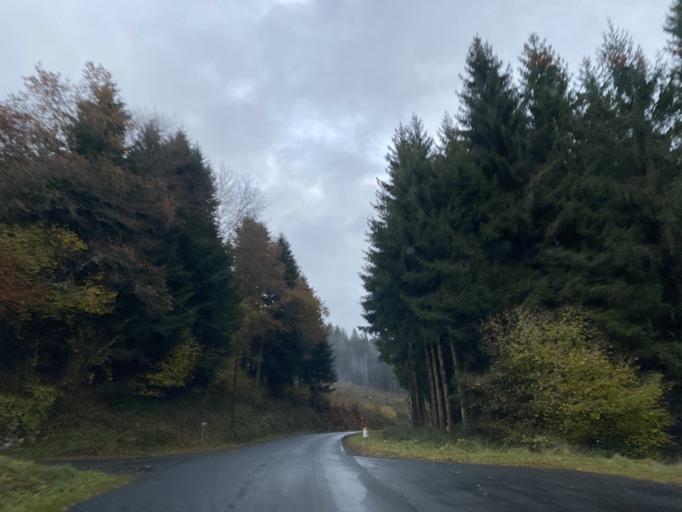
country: FR
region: Auvergne
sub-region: Departement du Puy-de-Dome
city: Cunlhat
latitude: 45.5873
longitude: 3.5614
